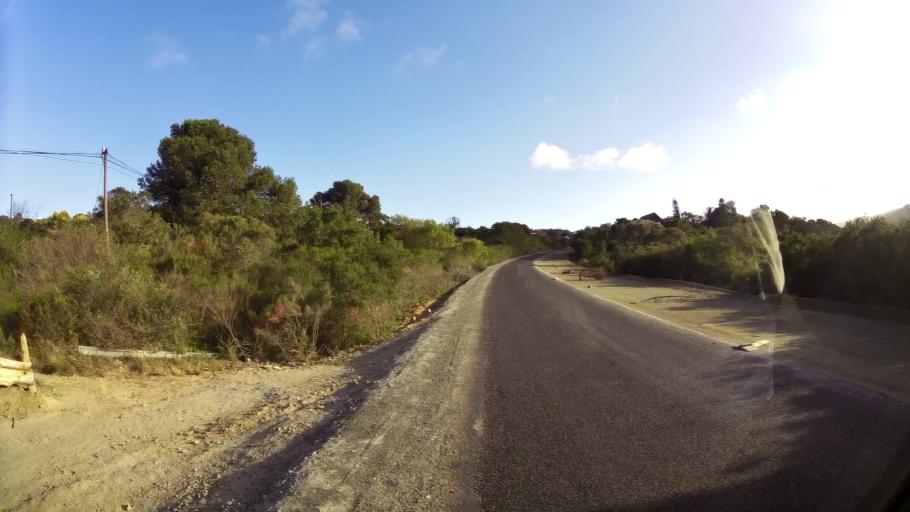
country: ZA
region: Western Cape
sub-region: Eden District Municipality
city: George
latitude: -33.9946
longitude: 22.6174
